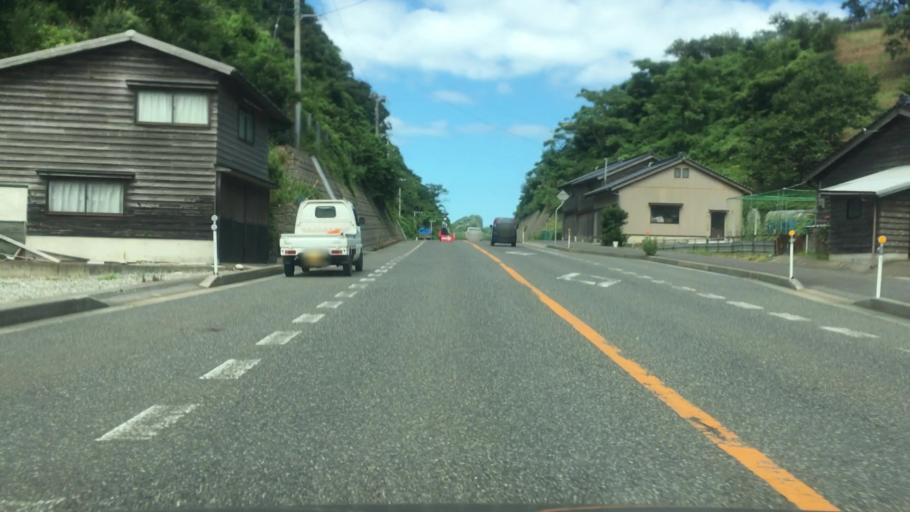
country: JP
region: Tottori
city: Tottori
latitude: 35.6169
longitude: 134.4106
